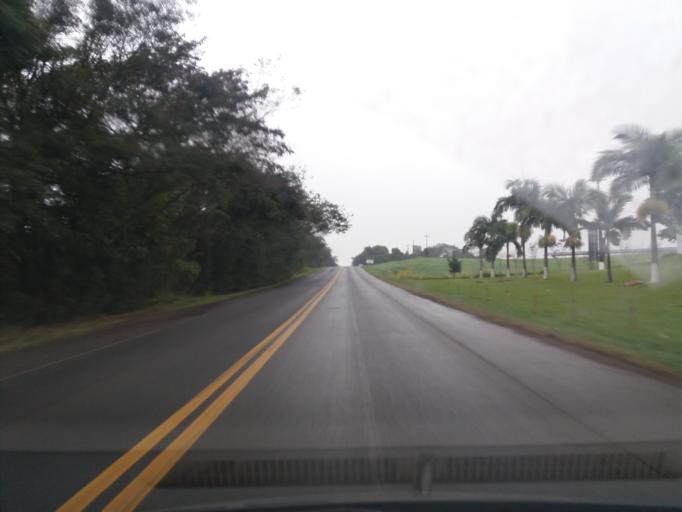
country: BR
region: Parana
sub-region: Ampere
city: Ampere
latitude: -25.8890
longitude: -53.4652
